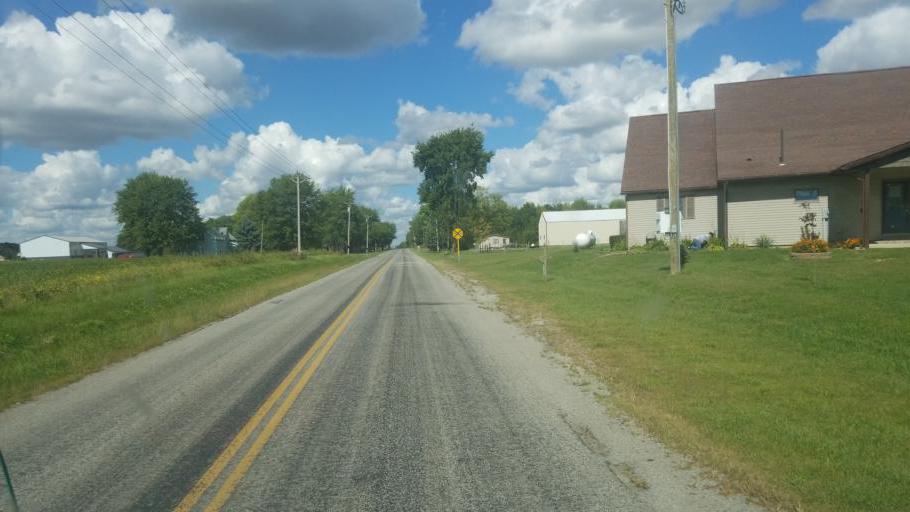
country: US
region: Ohio
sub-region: Champaign County
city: North Lewisburg
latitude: 40.3658
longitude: -83.5112
